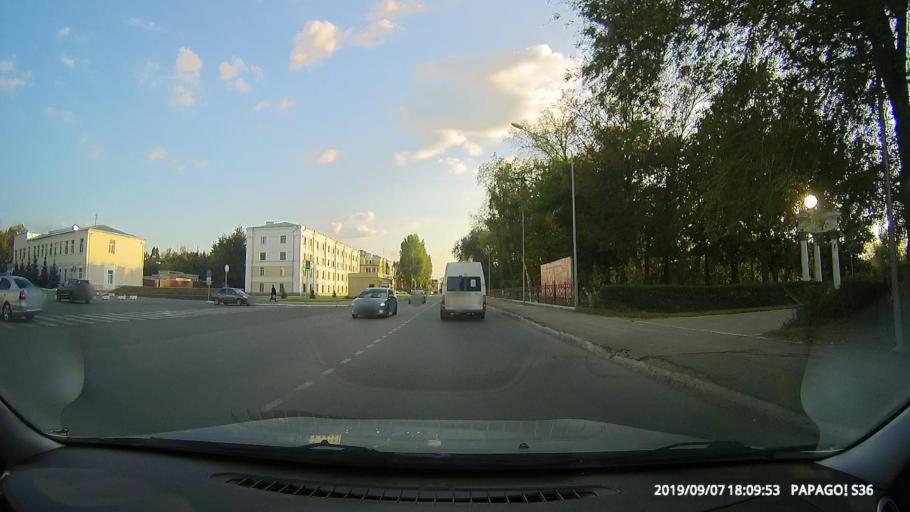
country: RU
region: Samara
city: Chapayevsk
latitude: 52.9973
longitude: 49.7676
